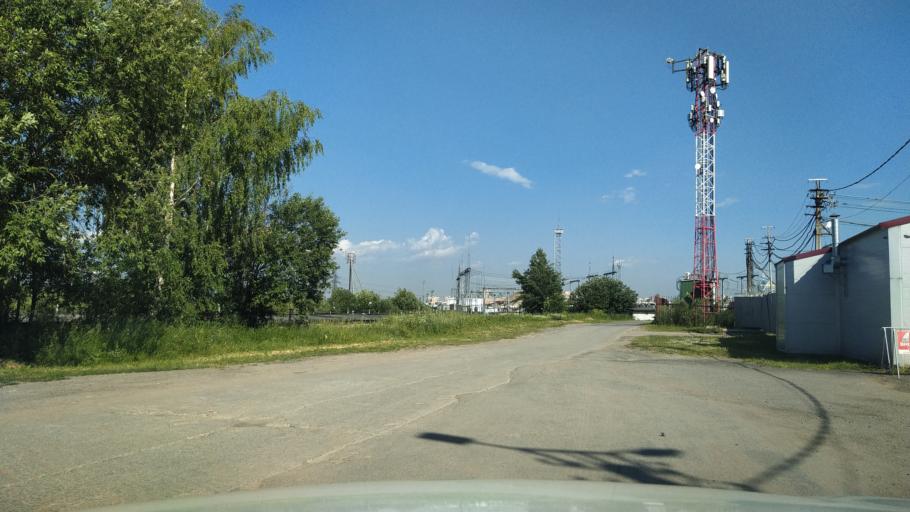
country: RU
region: St.-Petersburg
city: Uritsk
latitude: 59.8639
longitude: 30.2108
